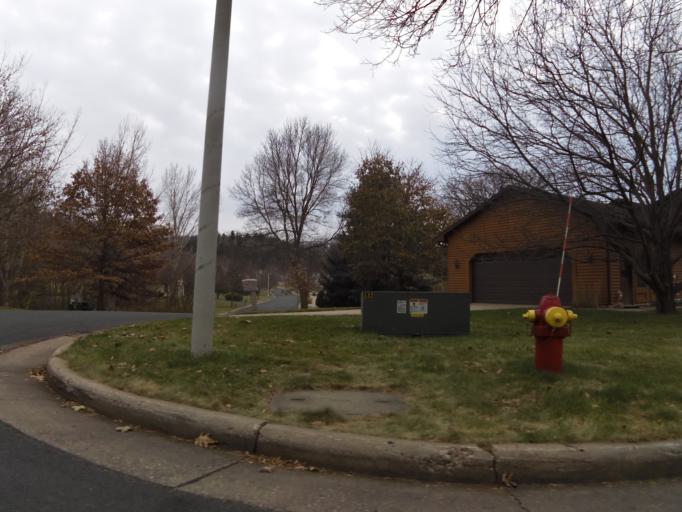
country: US
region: Wisconsin
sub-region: Pierce County
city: River Falls
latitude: 44.8594
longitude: -92.6027
